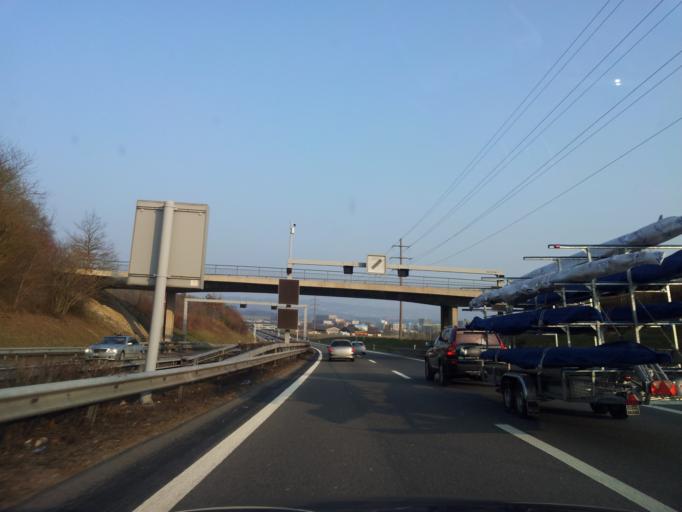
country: CH
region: Aargau
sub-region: Bezirk Brugg
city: Hausen
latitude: 47.4518
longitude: 8.1924
